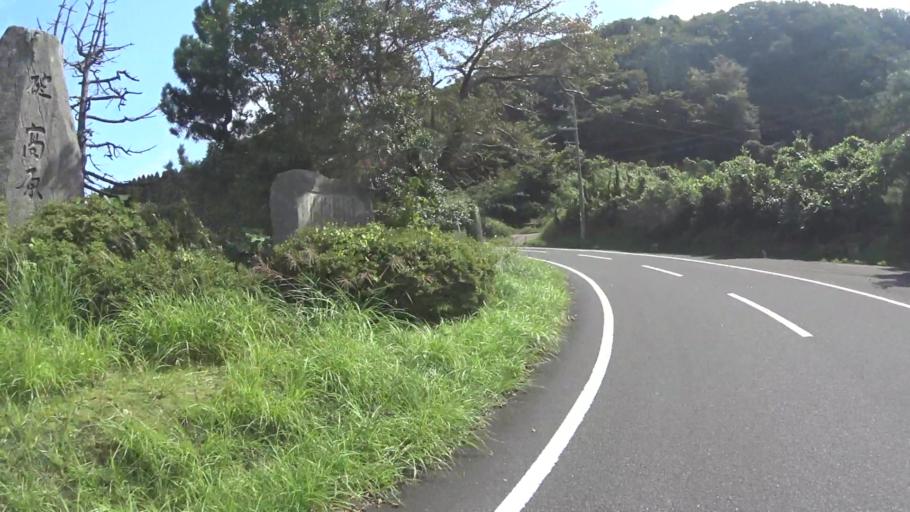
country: JP
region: Kyoto
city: Miyazu
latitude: 35.7194
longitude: 135.1866
